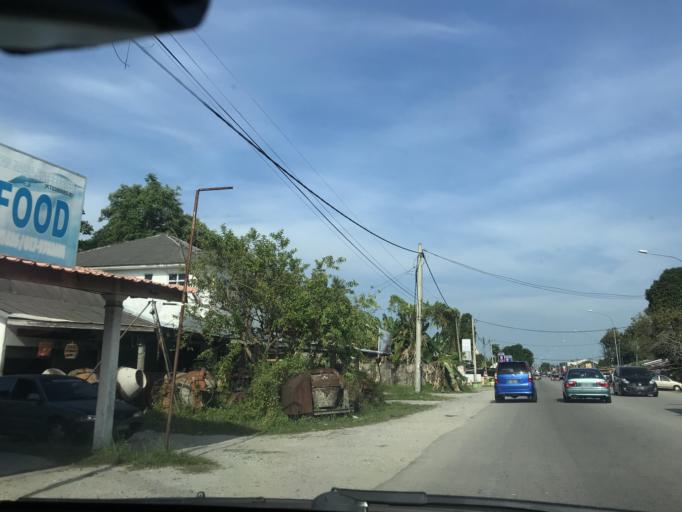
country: MY
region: Kelantan
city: Kota Bharu
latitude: 6.1221
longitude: 102.2833
